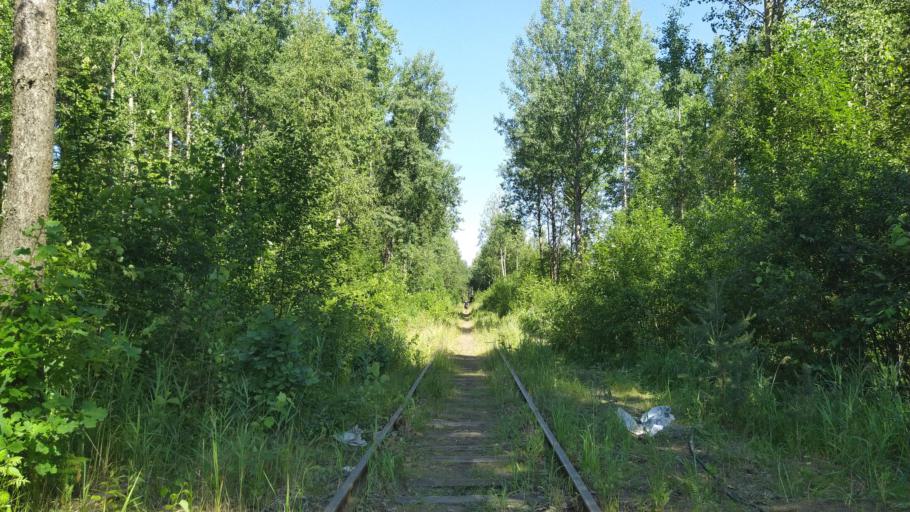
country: RU
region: St.-Petersburg
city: Bol'shaya Izhora
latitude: 59.9174
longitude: 29.5786
